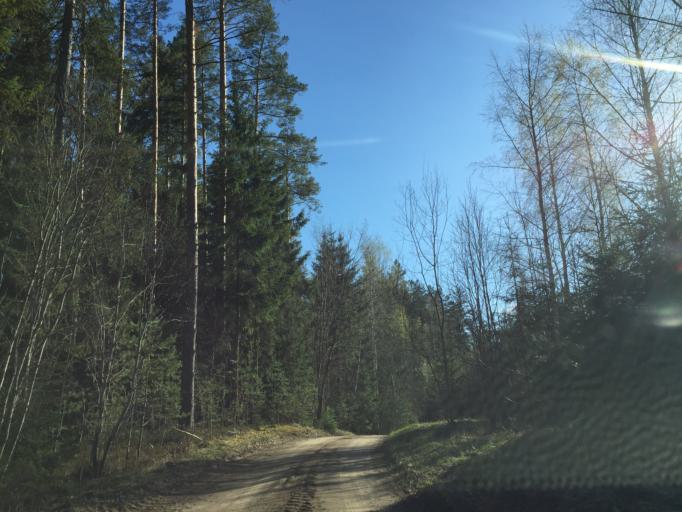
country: EE
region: Valgamaa
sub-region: Valga linn
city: Valga
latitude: 57.7831
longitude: 26.2444
